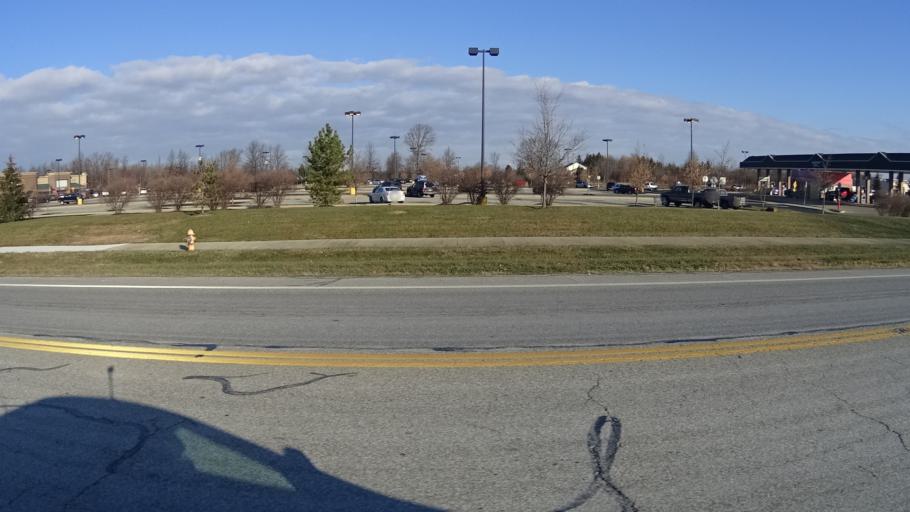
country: US
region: Ohio
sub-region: Lorain County
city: Oberlin
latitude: 41.2653
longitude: -82.2215
